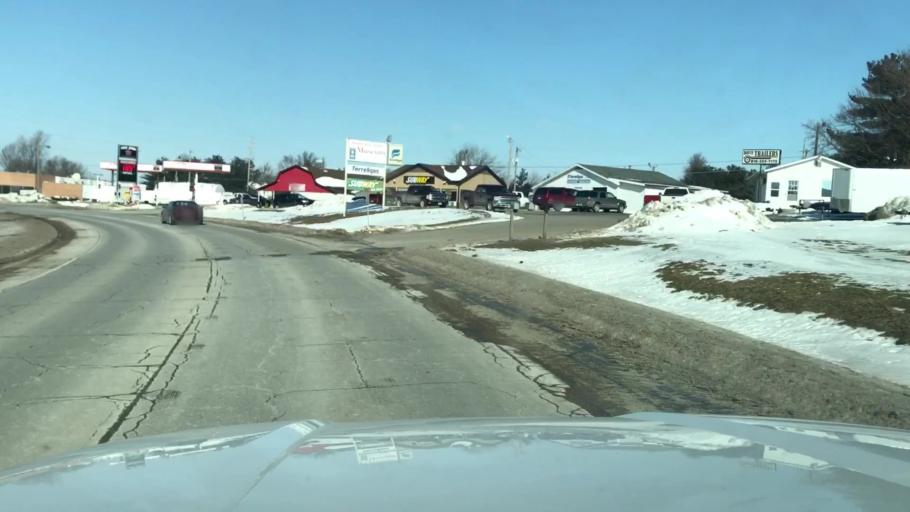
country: US
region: Missouri
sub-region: Andrew County
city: Savannah
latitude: 39.9458
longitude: -94.8220
